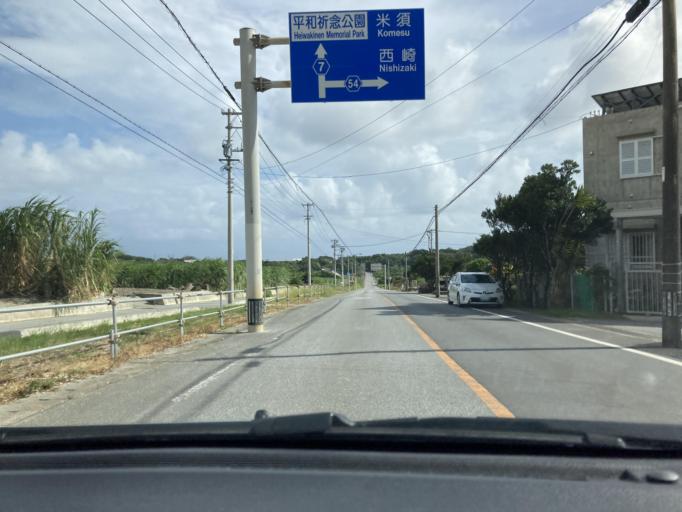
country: JP
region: Okinawa
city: Itoman
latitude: 26.1031
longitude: 127.6963
